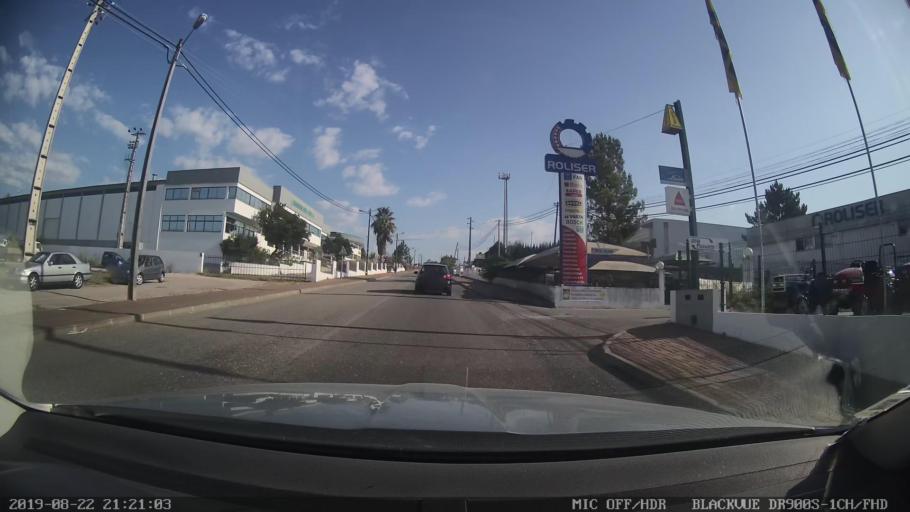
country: PT
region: Castelo Branco
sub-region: Serta
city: Serta
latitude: 39.8161
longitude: -8.1089
